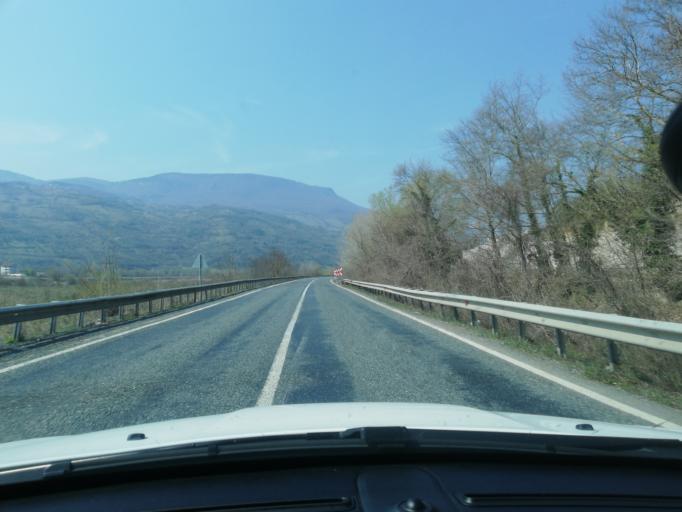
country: TR
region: Karabuk
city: Yenice
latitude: 41.2168
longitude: 32.2881
